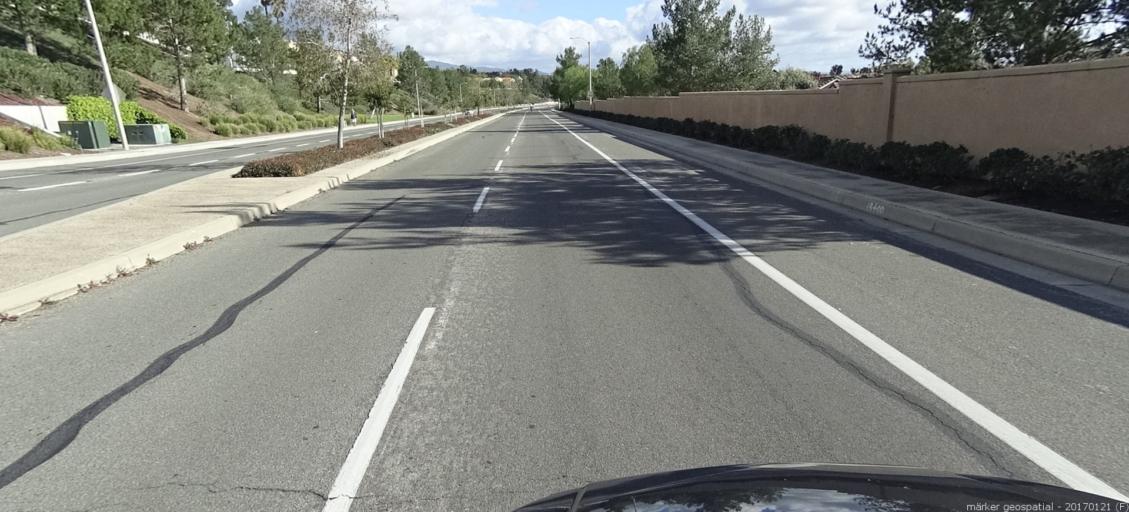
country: US
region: California
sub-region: Orange County
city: Foothill Ranch
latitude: 33.6859
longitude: -117.6715
